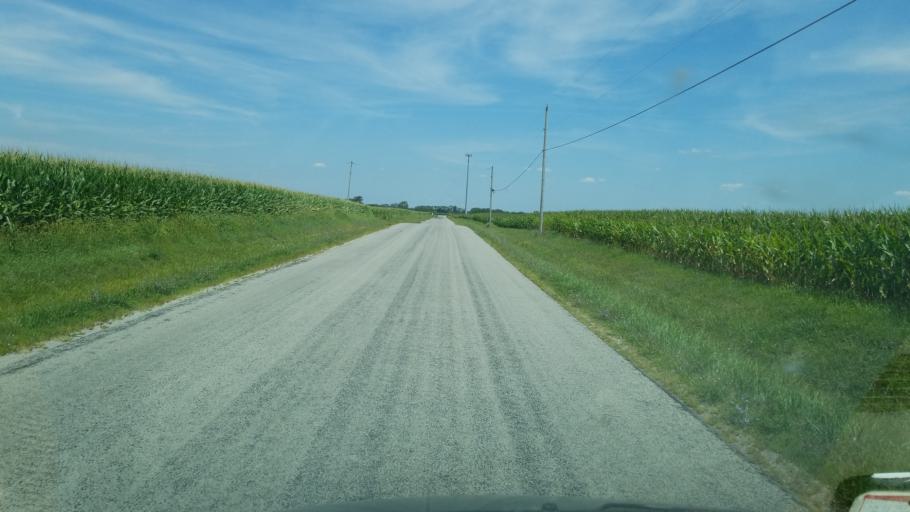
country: US
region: Ohio
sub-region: Madison County
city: West Jefferson
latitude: 39.9170
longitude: -83.2971
